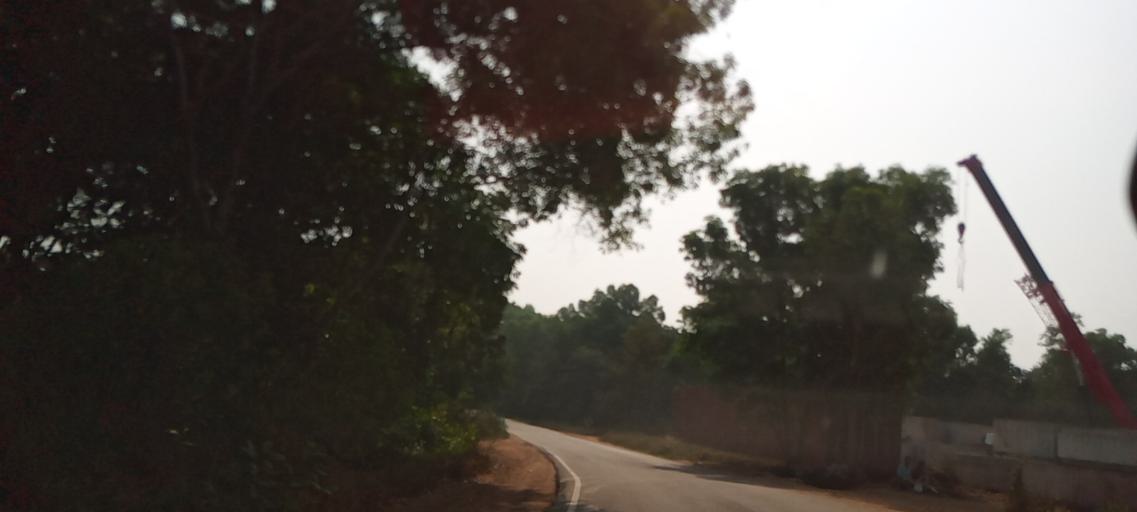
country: IN
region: Karnataka
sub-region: Udupi
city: Coondapoor
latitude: 13.5142
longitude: 74.7959
